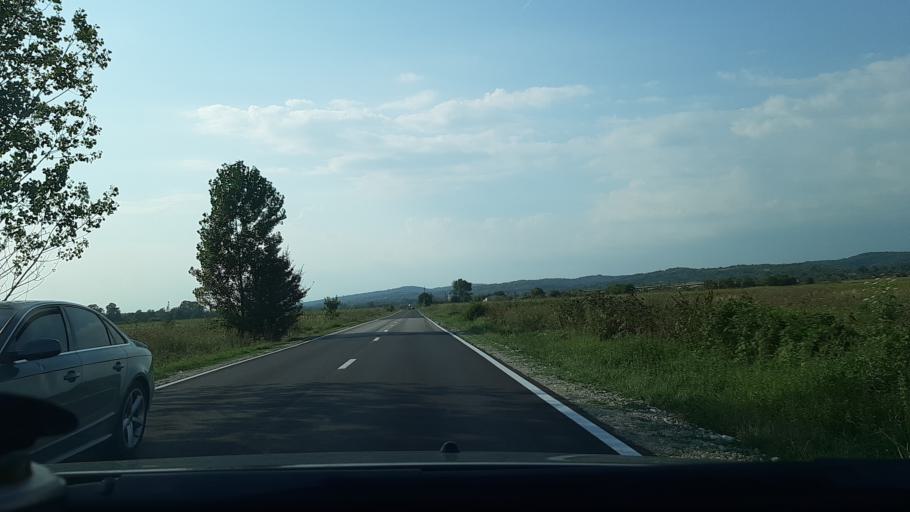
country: RO
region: Gorj
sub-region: Comuna Targu Carbunesti
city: Pojogeni
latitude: 45.0101
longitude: 23.4775
